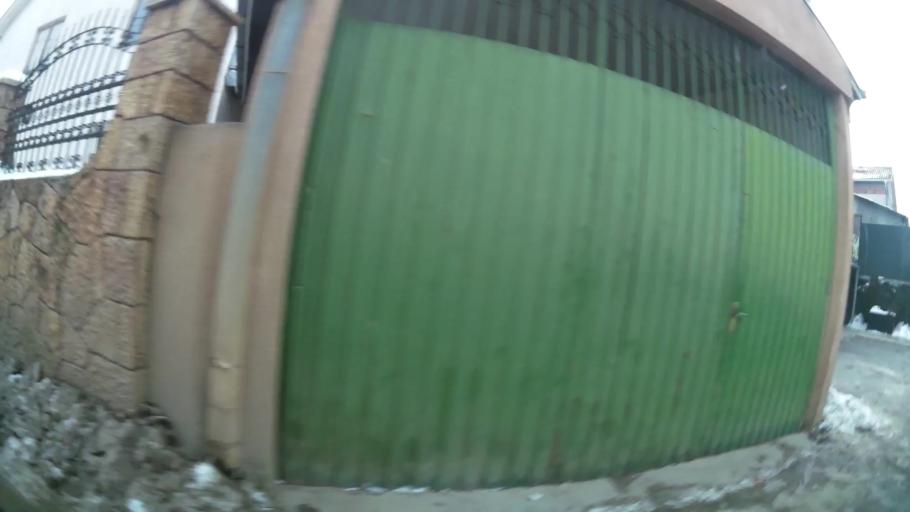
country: MK
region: Suto Orizari
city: Suto Orizare
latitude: 42.0345
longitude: 21.4154
